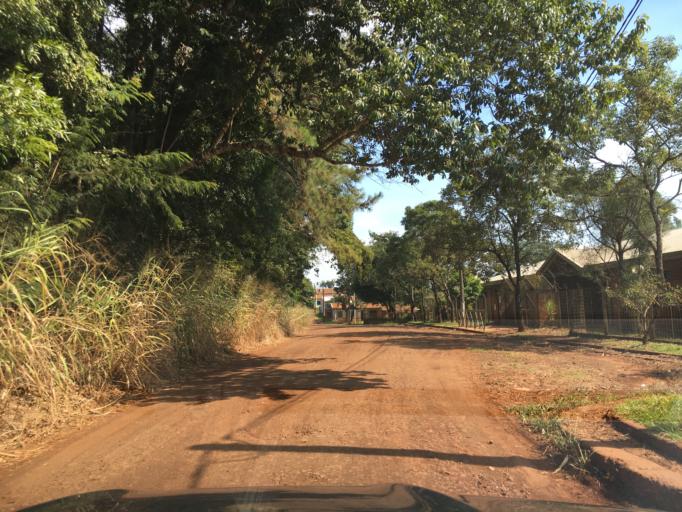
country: AR
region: Misiones
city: Puerto Rico
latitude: -26.8048
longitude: -54.9976
